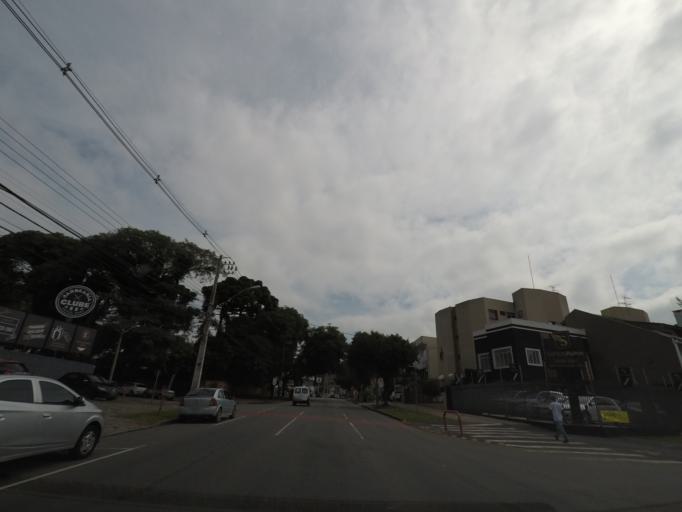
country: BR
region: Parana
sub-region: Curitiba
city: Curitiba
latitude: -25.4535
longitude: -49.2749
